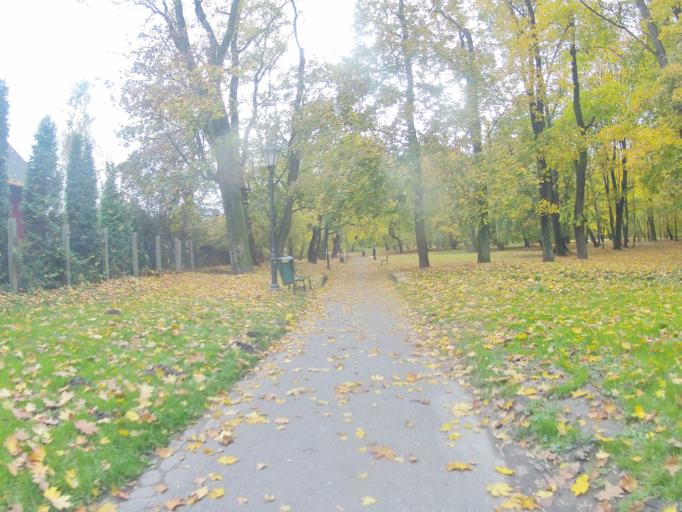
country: PL
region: Lesser Poland Voivodeship
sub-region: Powiat krakowski
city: Rzaska
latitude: 50.0656
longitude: 19.8744
